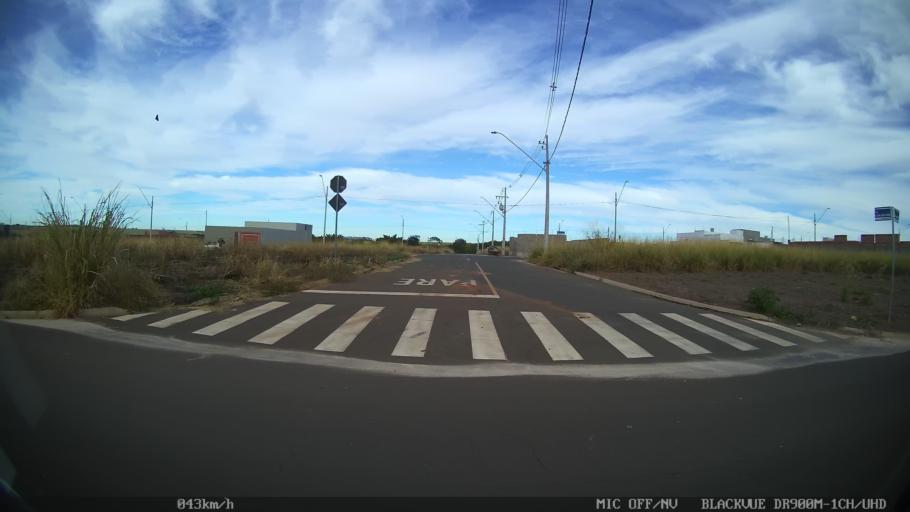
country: BR
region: Sao Paulo
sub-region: Catanduva
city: Catanduva
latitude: -21.1374
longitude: -49.0120
